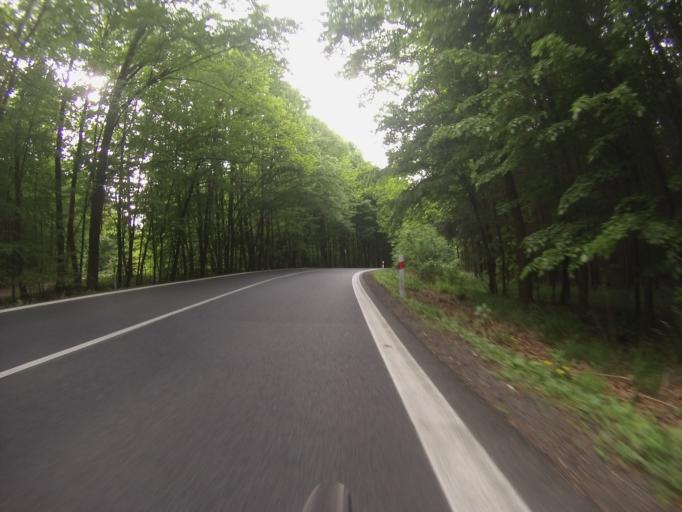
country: CZ
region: South Moravian
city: Veverska Bityska
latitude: 49.2564
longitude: 16.4736
